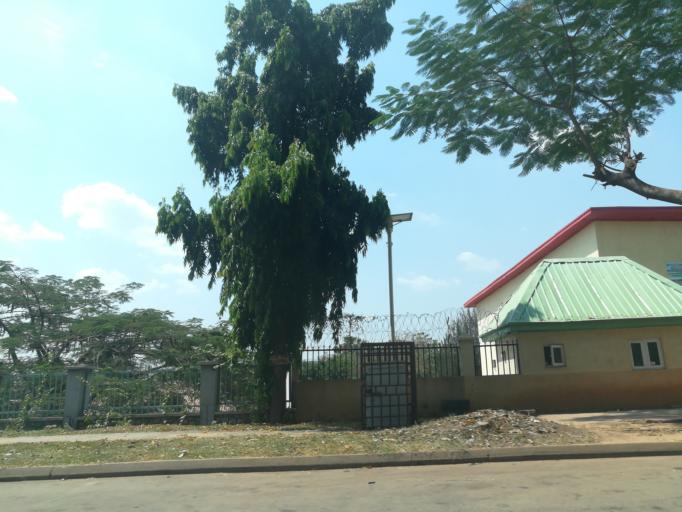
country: NG
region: Abuja Federal Capital Territory
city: Abuja
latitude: 9.0653
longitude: 7.4373
